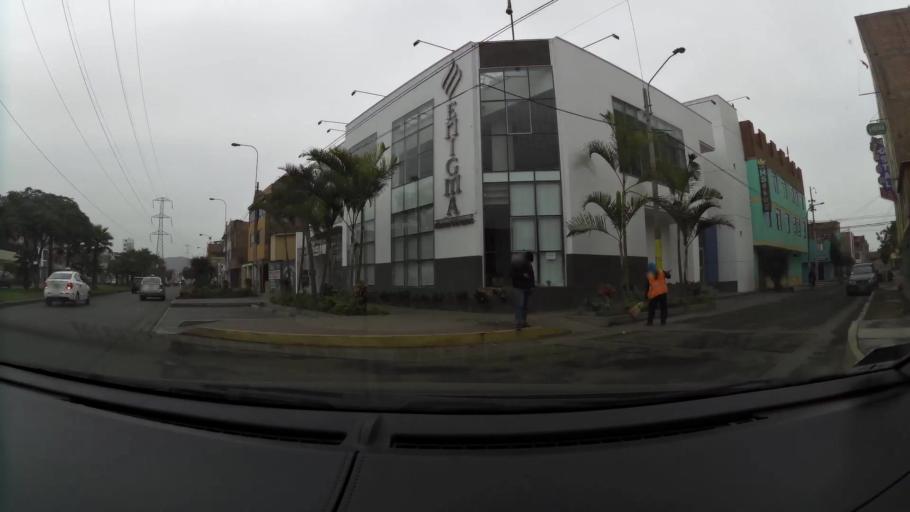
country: PE
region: Lima
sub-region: Lima
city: Independencia
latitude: -11.9751
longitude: -77.0725
